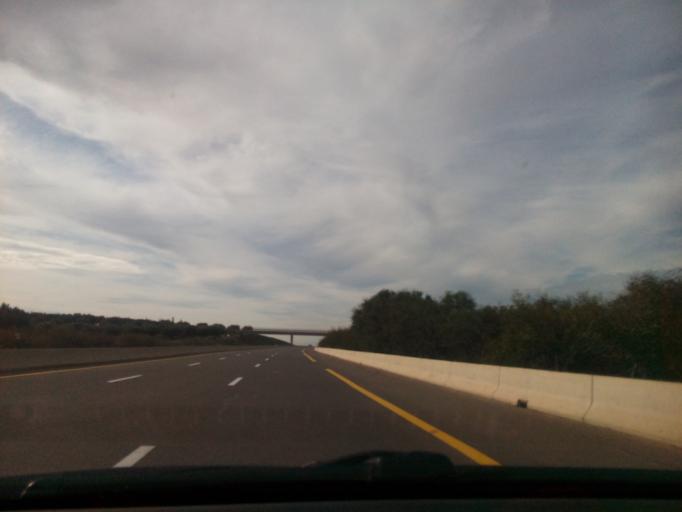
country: DZ
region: Sidi Bel Abbes
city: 'Ain el Berd
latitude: 35.3384
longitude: -0.5191
